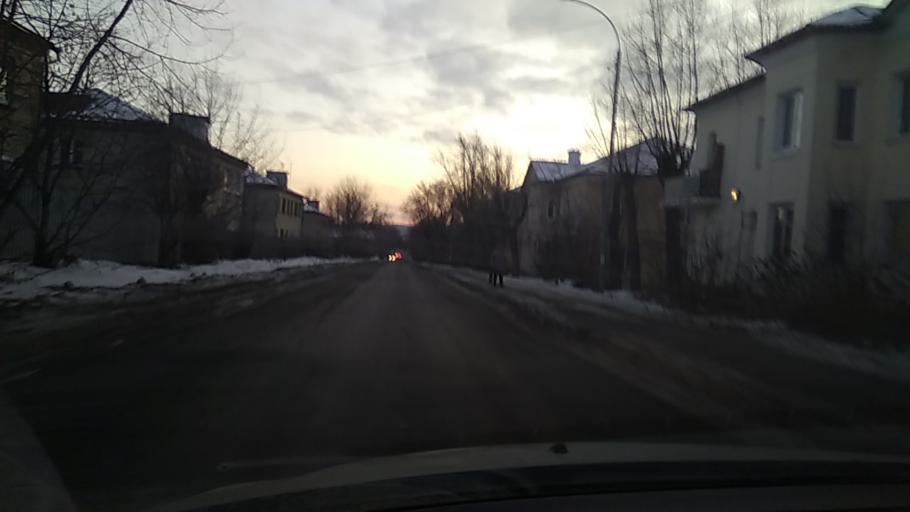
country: RU
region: Sverdlovsk
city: Istok
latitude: 56.7616
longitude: 60.7117
